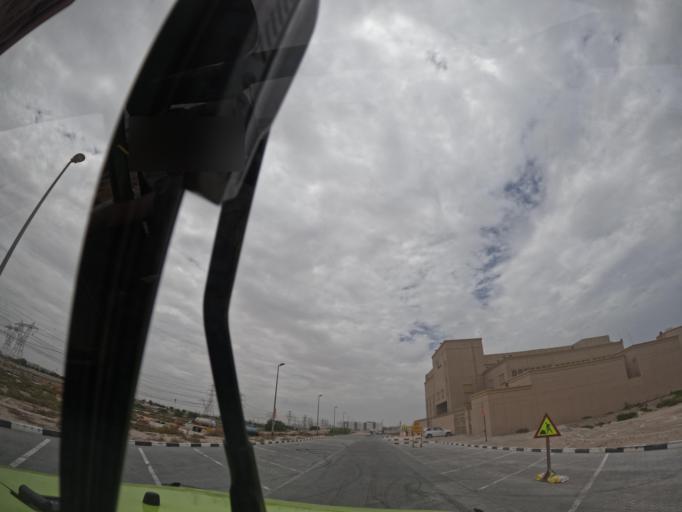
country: AE
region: Ash Shariqah
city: Sharjah
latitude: 25.1874
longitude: 55.3862
